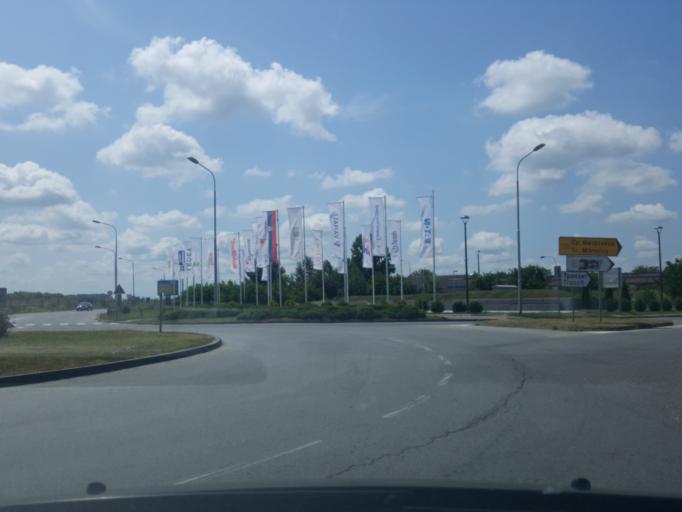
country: RS
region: Autonomna Pokrajina Vojvodina
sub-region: Sremski Okrug
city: Sremska Mitrovica
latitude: 44.9707
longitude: 19.6369
